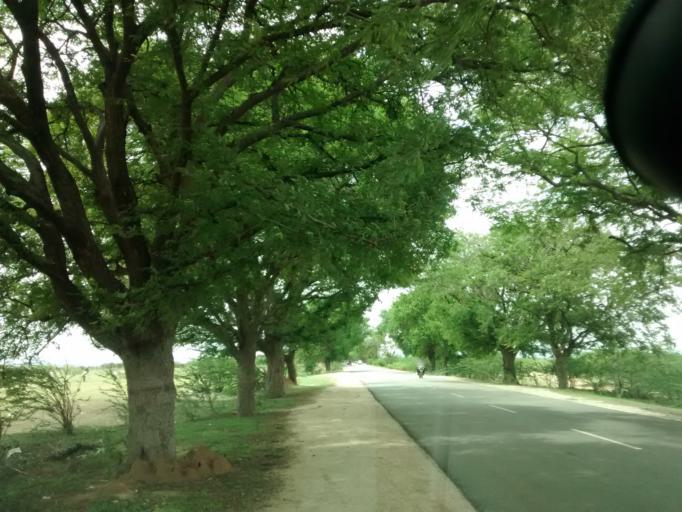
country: IN
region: Andhra Pradesh
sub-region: Anantapur
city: Hindupur
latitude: 13.8245
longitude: 77.5455
